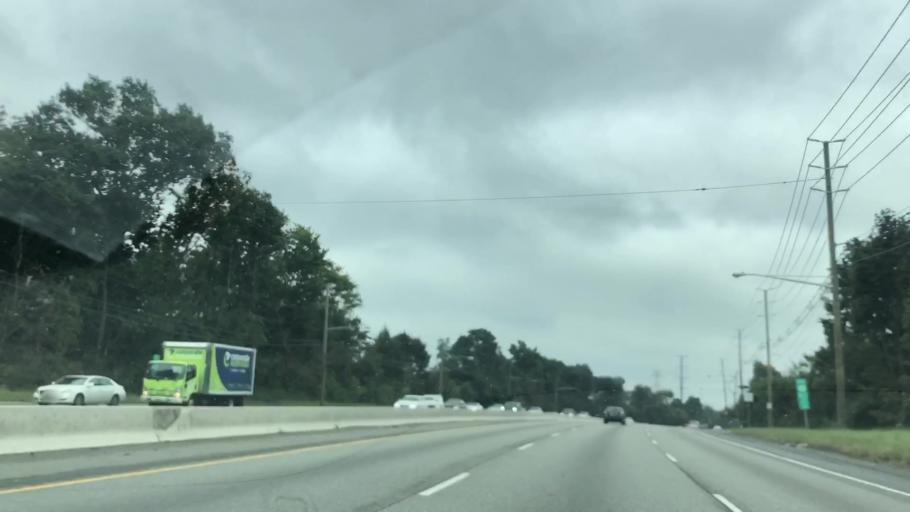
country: US
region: New Jersey
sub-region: Passaic County
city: Clifton
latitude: 40.8644
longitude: -74.1818
